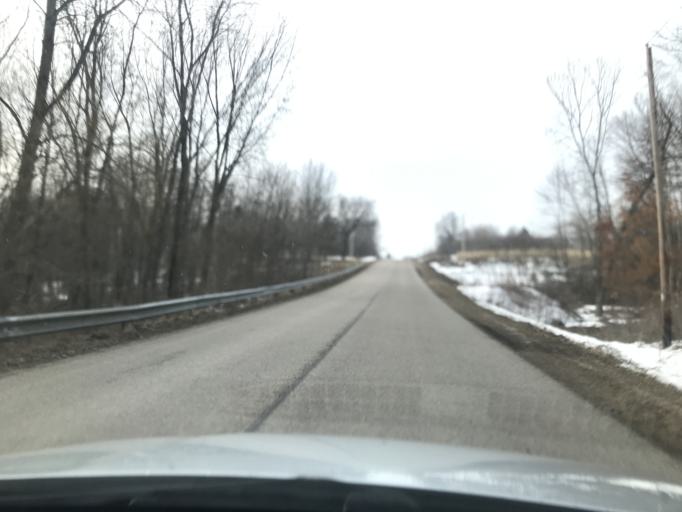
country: US
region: Wisconsin
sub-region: Oconto County
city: Oconto Falls
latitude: 44.8614
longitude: -88.1468
